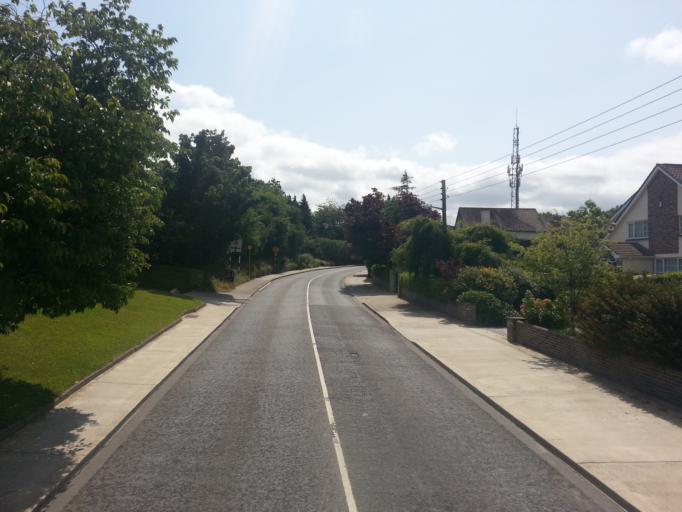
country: IE
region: Leinster
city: Sandyford
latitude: 53.2546
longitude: -6.2148
